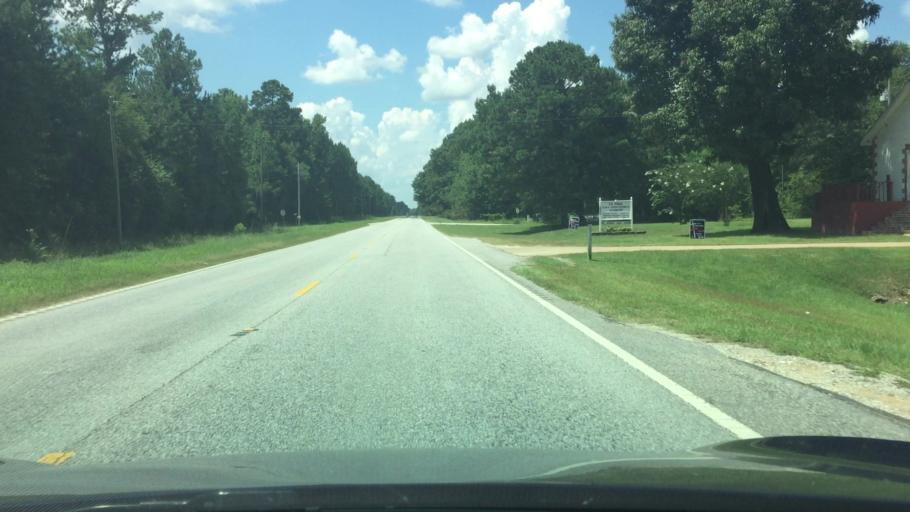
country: US
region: Alabama
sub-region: Montgomery County
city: Pike Road
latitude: 32.3907
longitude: -85.9787
